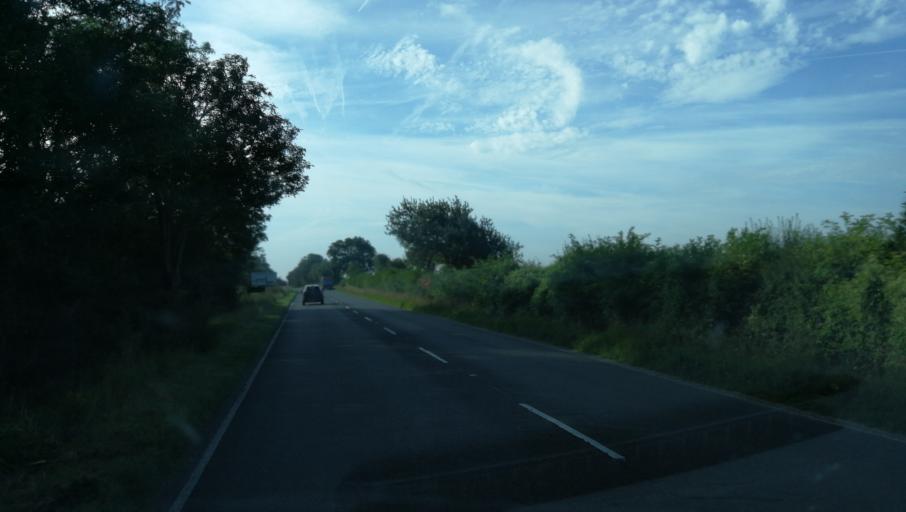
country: GB
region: England
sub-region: Oxfordshire
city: Woodstock
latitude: 51.8650
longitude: -1.3253
